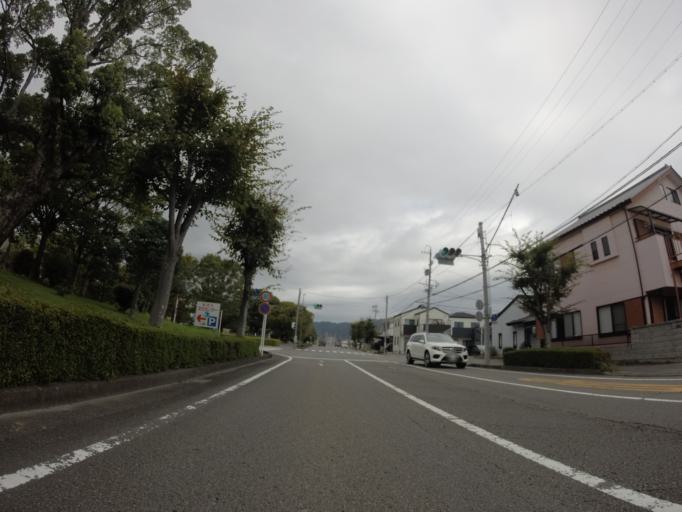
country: JP
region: Shizuoka
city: Yaizu
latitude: 34.8645
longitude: 138.3070
